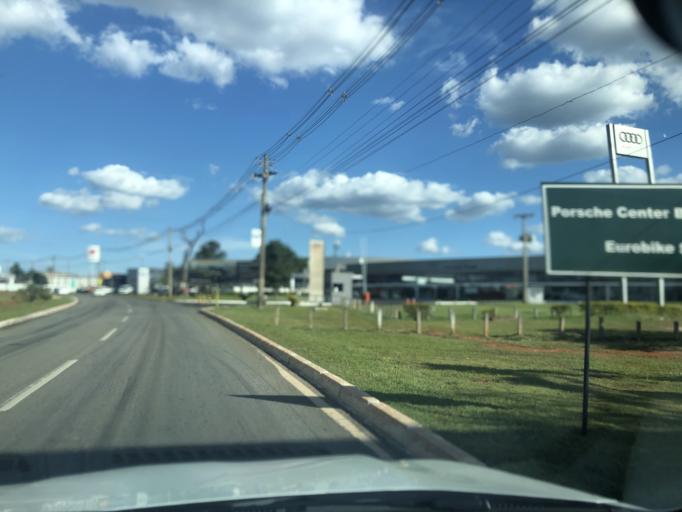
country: BR
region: Federal District
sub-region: Brasilia
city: Brasilia
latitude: -15.8694
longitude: -47.9364
